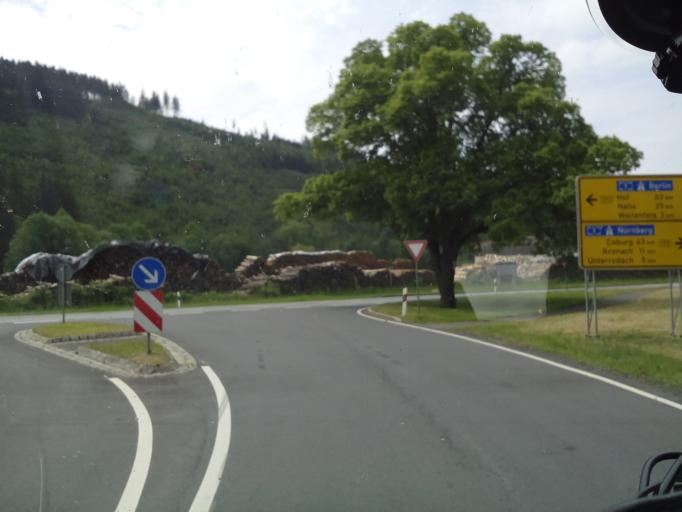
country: DE
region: Bavaria
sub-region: Upper Franconia
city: Steinwiesen
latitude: 50.2797
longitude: 11.4302
